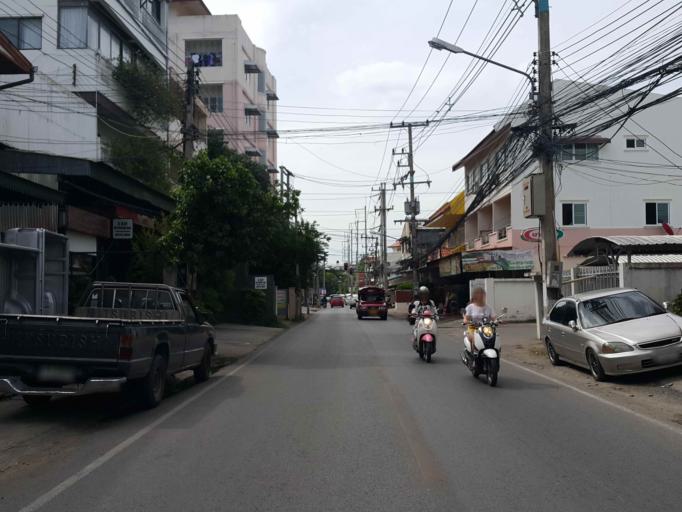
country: TH
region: Chiang Mai
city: Chiang Mai
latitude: 18.7767
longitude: 98.9961
